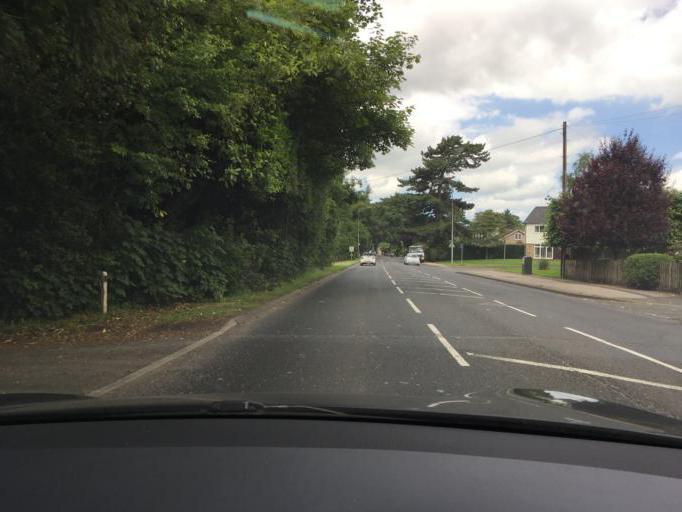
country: GB
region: England
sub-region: Cheshire East
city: Knutsford
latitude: 53.2971
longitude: -2.3606
